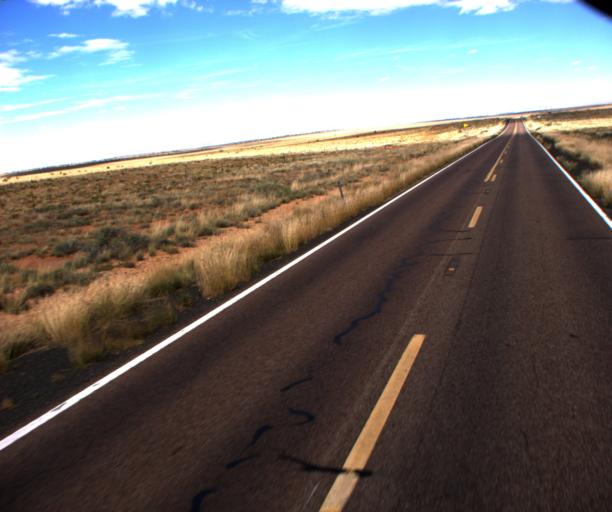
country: US
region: Arizona
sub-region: Navajo County
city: Holbrook
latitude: 34.7695
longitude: -110.2428
